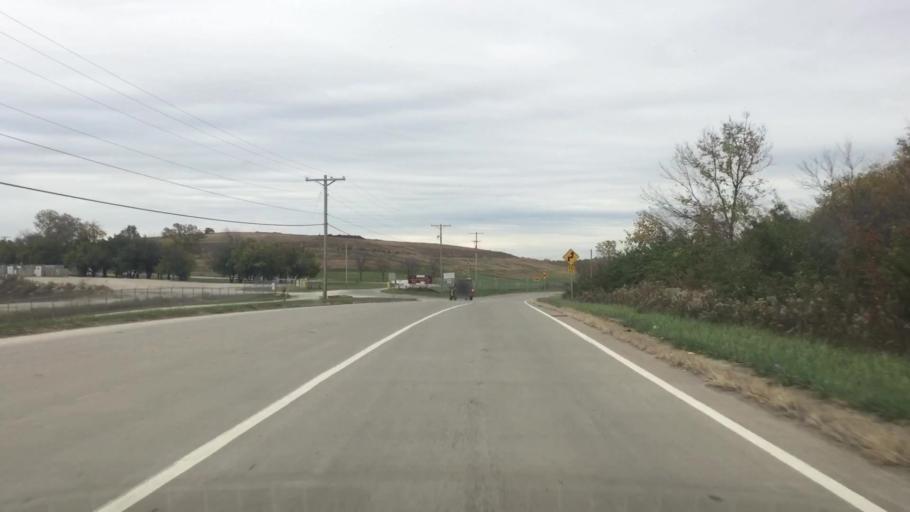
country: US
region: Missouri
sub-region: Jackson County
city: Greenwood
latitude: 38.8825
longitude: -94.3581
